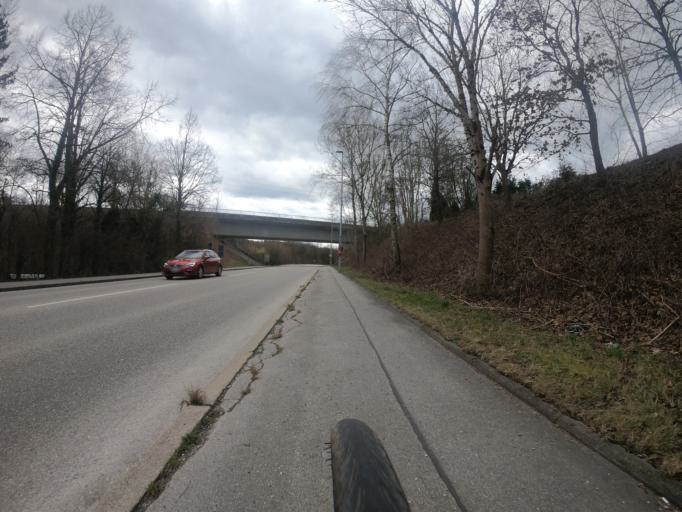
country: DE
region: Bavaria
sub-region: Upper Bavaria
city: Fuerstenfeldbruck
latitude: 48.1650
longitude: 11.2367
